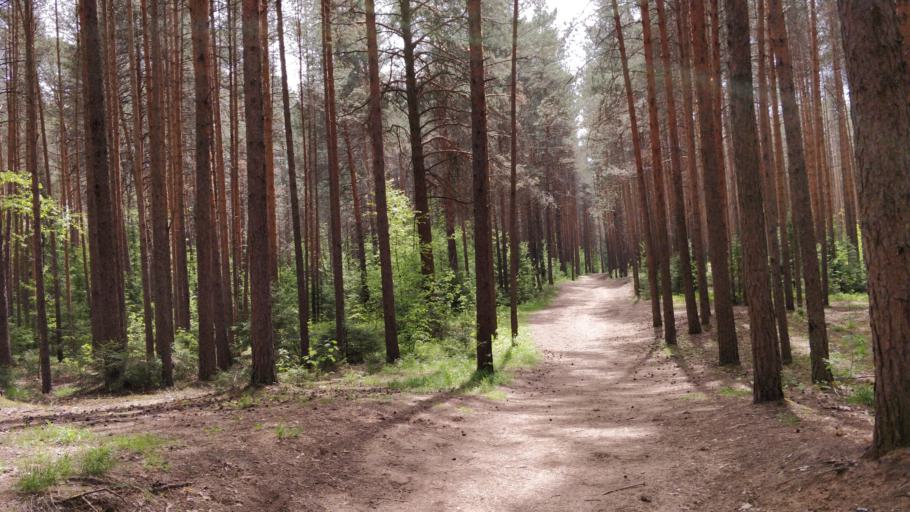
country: RU
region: Perm
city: Kondratovo
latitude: 57.9827
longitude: 56.1461
